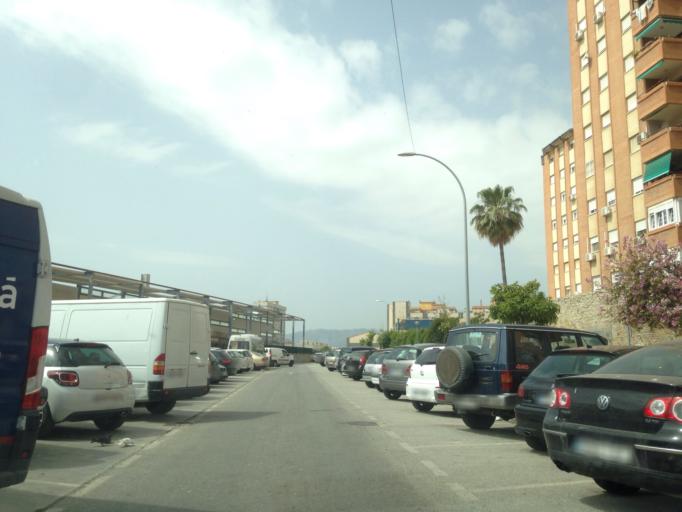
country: ES
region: Andalusia
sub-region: Provincia de Malaga
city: Malaga
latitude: 36.7088
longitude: -4.4395
